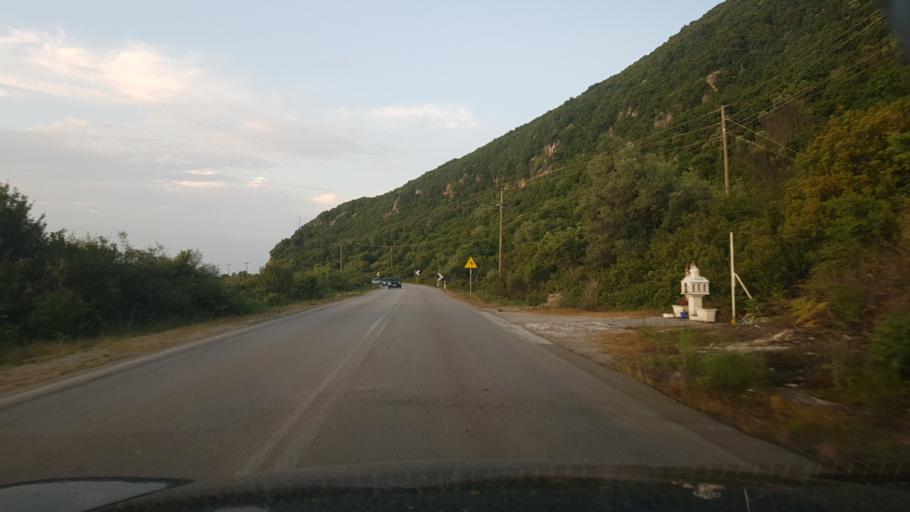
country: GR
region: Ionian Islands
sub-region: Lefkada
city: Lefkada
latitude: 38.8521
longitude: 20.7464
